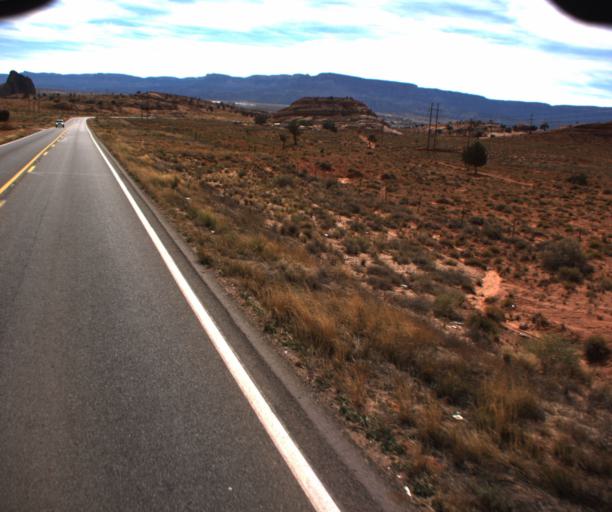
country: US
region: Arizona
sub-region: Navajo County
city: Kayenta
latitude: 36.7552
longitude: -110.2263
